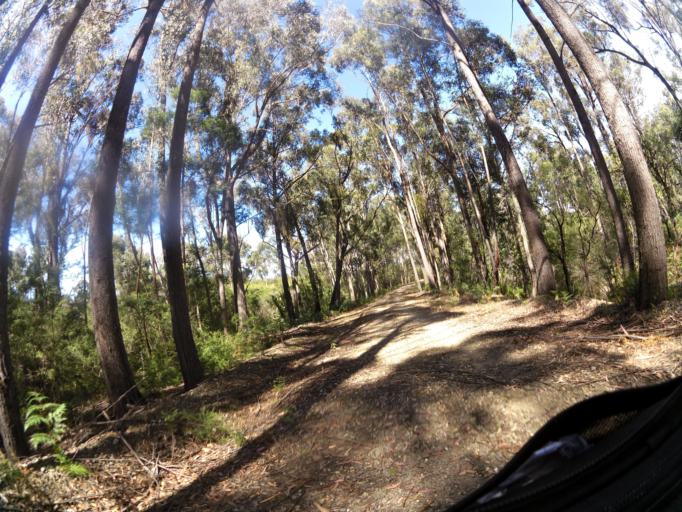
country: AU
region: Victoria
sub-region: East Gippsland
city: Lakes Entrance
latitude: -37.7188
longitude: 148.1288
